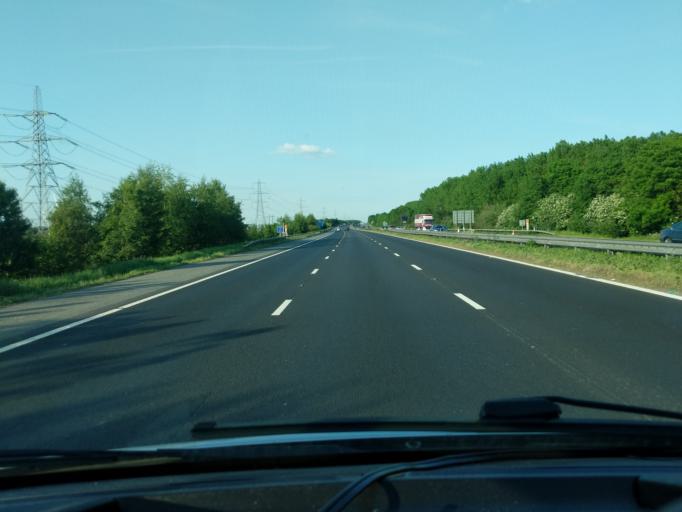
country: GB
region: England
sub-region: Cheshire West and Chester
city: Elton
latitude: 53.2702
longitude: -2.7935
